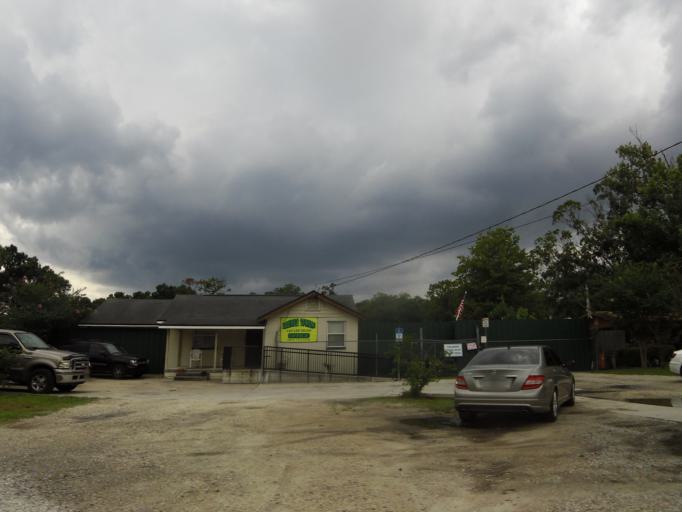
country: US
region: Florida
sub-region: Duval County
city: Jacksonville
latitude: 30.3251
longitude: -81.5361
